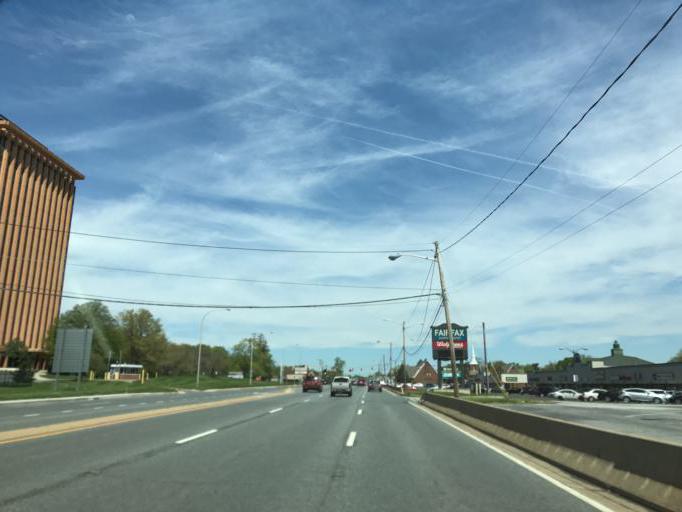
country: US
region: Delaware
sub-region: New Castle County
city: Wilmington
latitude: 39.7896
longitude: -75.5464
